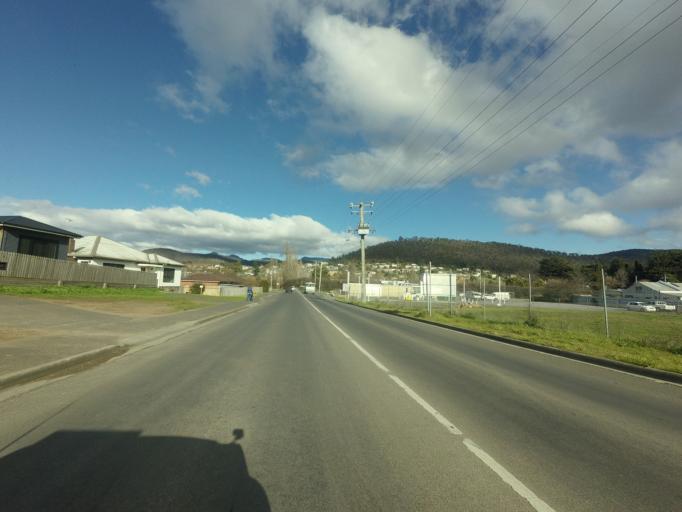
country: AU
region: Tasmania
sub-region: Derwent Valley
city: New Norfolk
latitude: -42.7767
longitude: 147.0537
